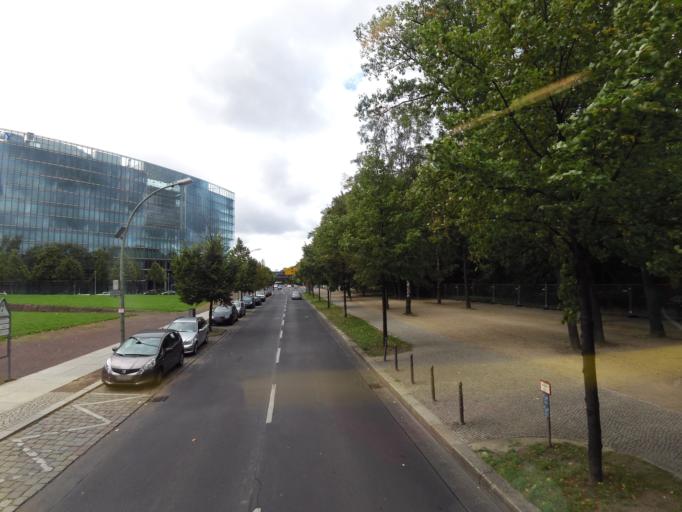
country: DE
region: Berlin
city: Tiergarten Bezirk
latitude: 52.5114
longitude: 13.3735
